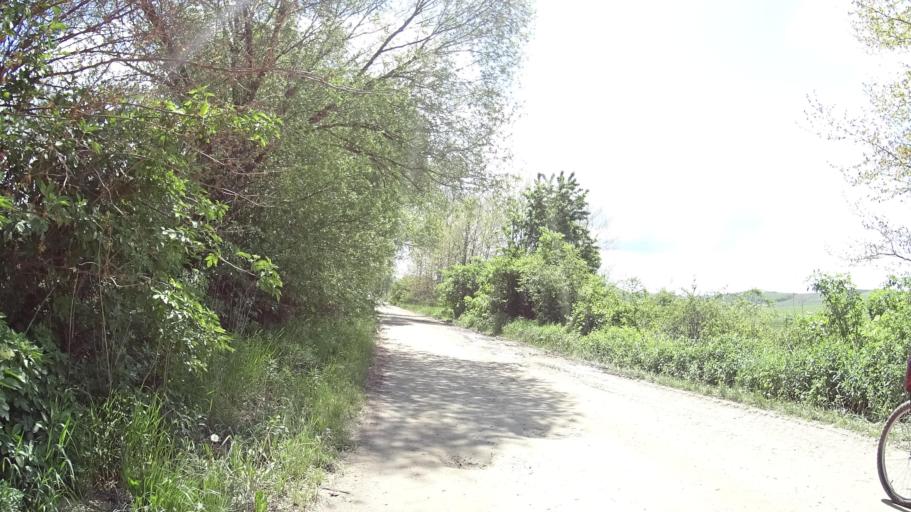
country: HU
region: Komarom-Esztergom
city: Kesztolc
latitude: 47.6934
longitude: 18.7997
